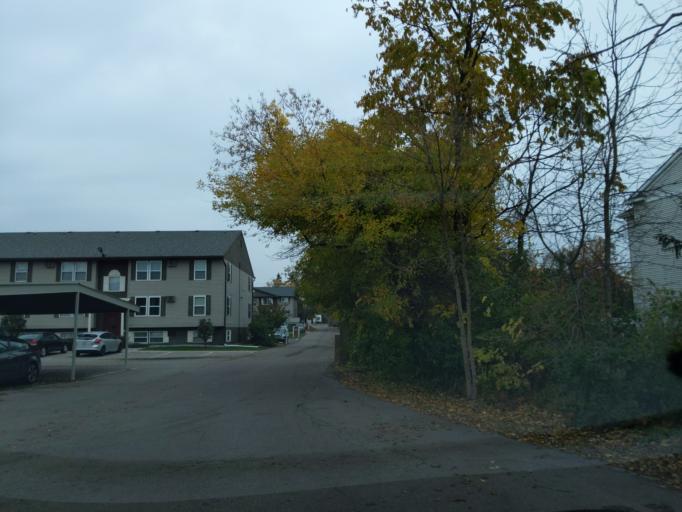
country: US
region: Michigan
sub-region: Ingham County
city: Edgemont Park
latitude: 42.7102
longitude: -84.5948
